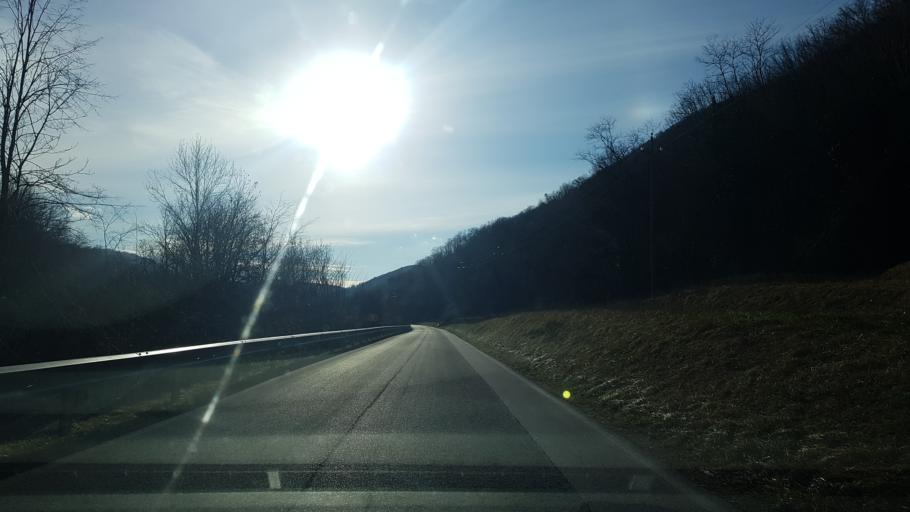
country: IT
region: Friuli Venezia Giulia
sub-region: Provincia di Udine
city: Savogna
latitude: 46.1403
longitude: 13.5425
